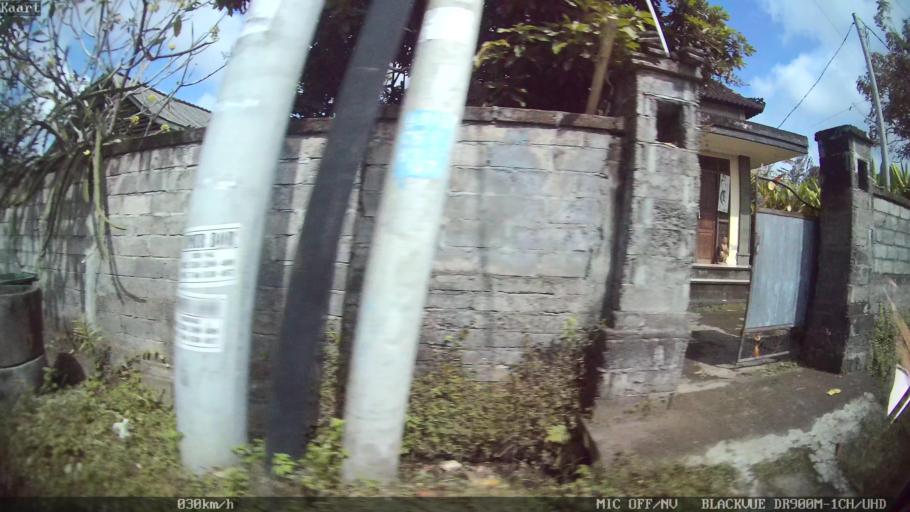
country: ID
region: Bali
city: Banjar Tebongkang
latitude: -8.5418
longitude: 115.2501
